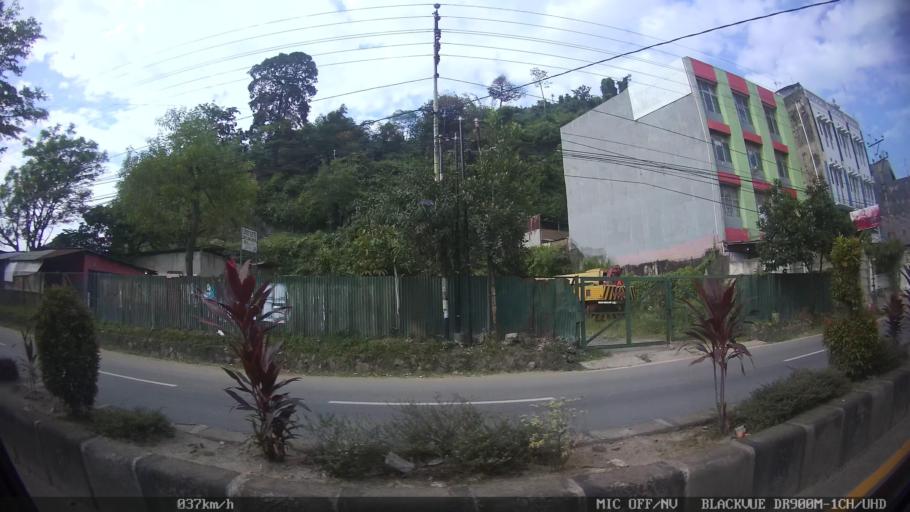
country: ID
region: Lampung
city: Bandarlampung
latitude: -5.4441
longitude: 105.2813
